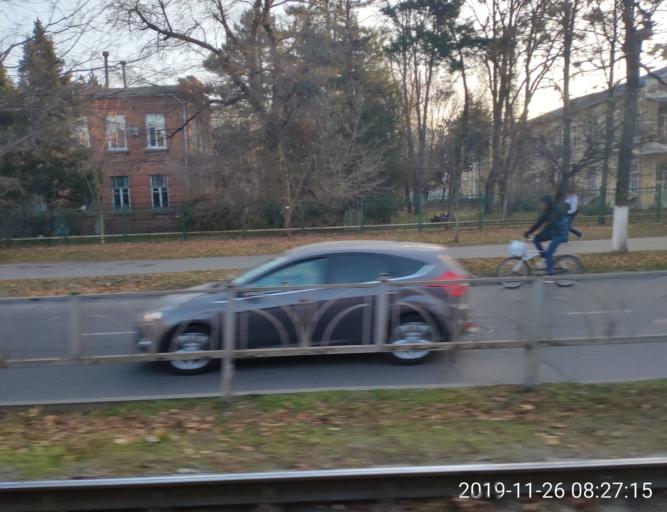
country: RU
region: Krasnodarskiy
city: Krasnodar
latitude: 45.0584
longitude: 39.0022
